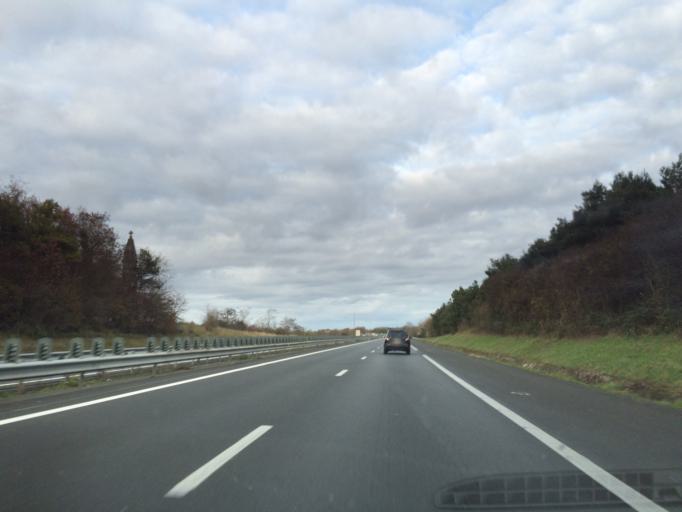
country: FR
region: Poitou-Charentes
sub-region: Departement de la Charente-Maritime
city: Saint-Jean-d'Angely
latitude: 46.0261
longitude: -0.5401
